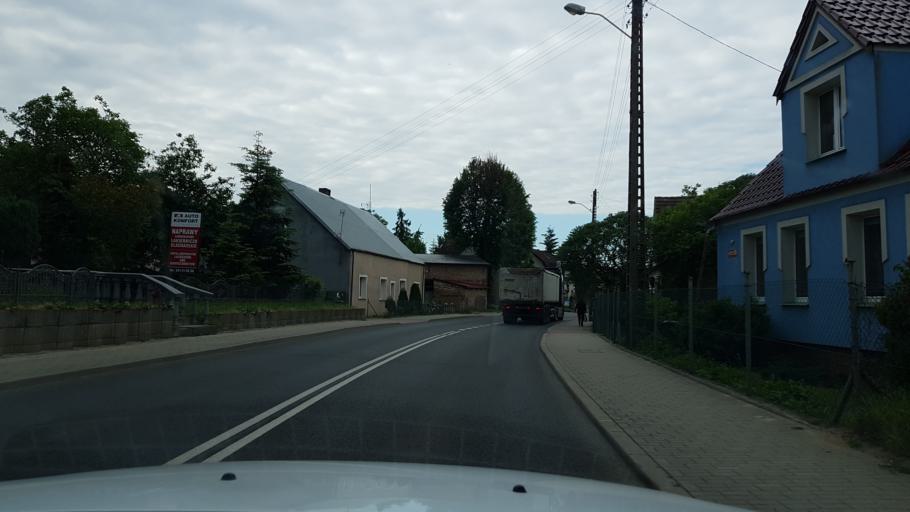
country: PL
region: West Pomeranian Voivodeship
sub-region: Powiat gryfinski
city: Gryfino
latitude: 53.2809
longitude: 14.5145
